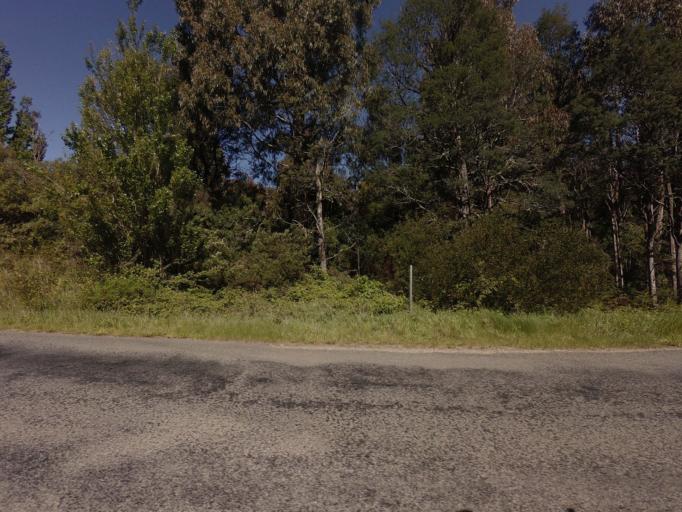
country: AU
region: Tasmania
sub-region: Derwent Valley
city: New Norfolk
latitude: -42.7506
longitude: 146.6420
